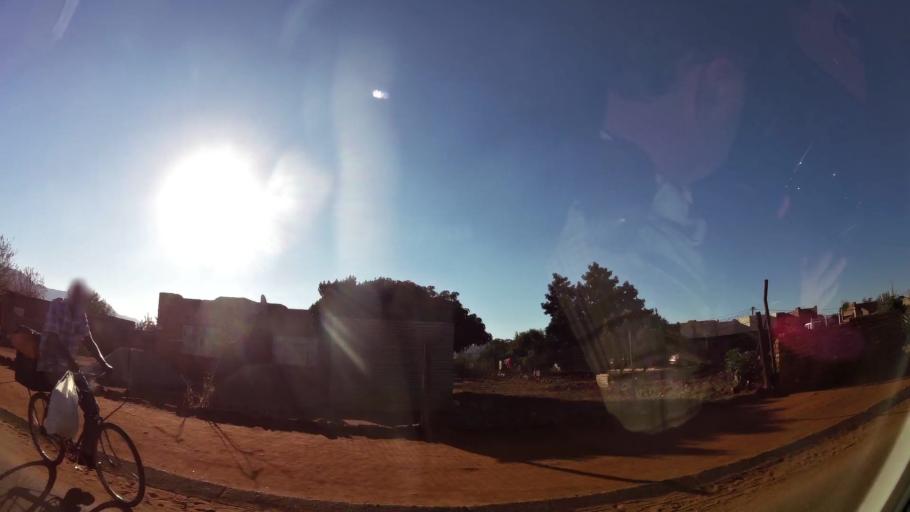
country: ZA
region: Limpopo
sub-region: Waterberg District Municipality
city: Mokopane
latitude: -24.1785
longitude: 28.9775
